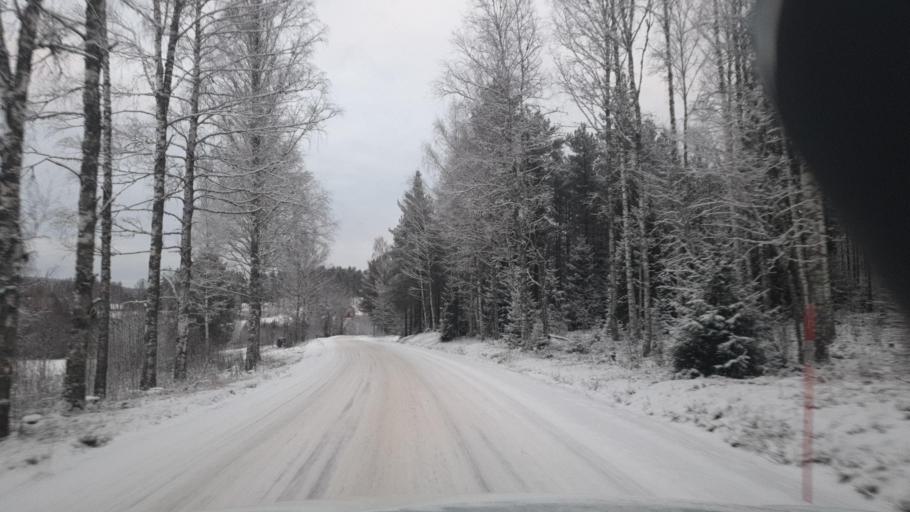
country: SE
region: Vaermland
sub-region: Eda Kommun
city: Charlottenberg
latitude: 59.7870
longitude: 12.2182
